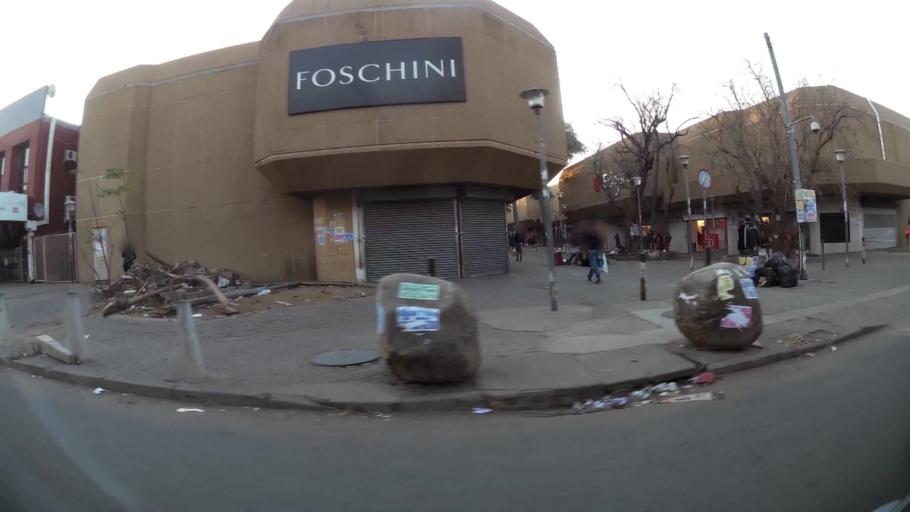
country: ZA
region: North-West
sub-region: Bojanala Platinum District Municipality
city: Rustenburg
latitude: -25.6684
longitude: 27.2420
